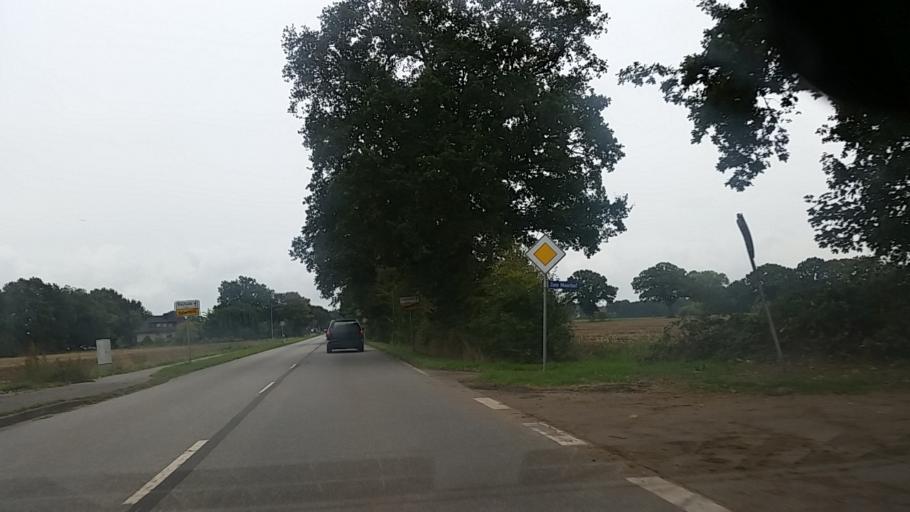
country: DE
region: Schleswig-Holstein
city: Kayhude
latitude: 53.7647
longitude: 10.1272
